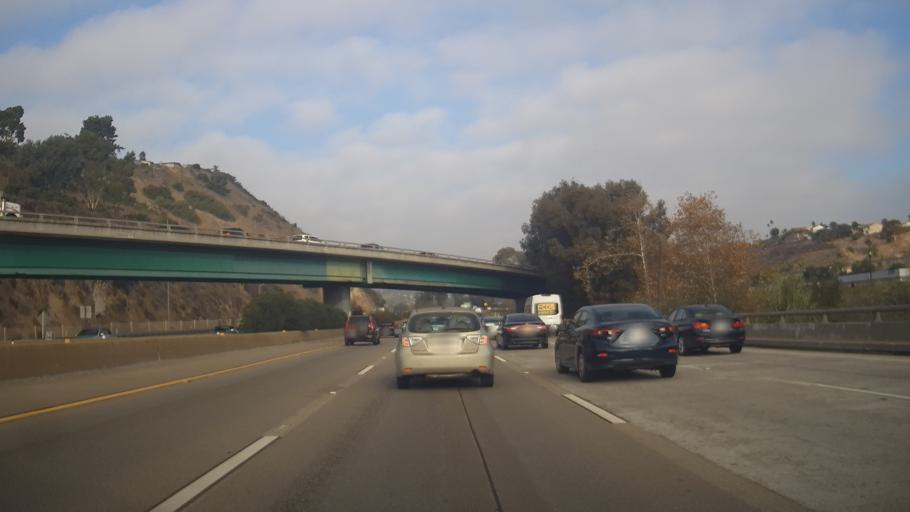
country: US
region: California
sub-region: San Diego County
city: La Jolla
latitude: 32.8114
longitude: -117.2195
